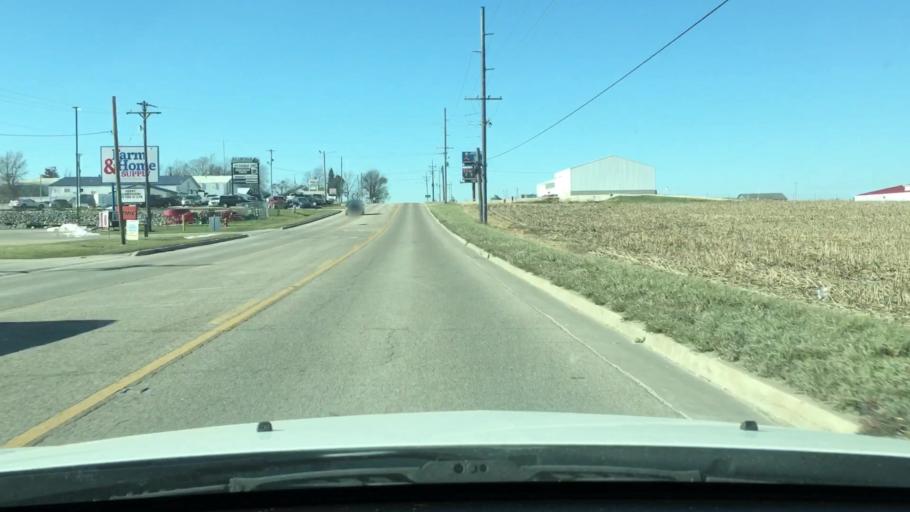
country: US
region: Illinois
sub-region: Pike County
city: Pittsfield
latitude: 39.6047
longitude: -90.8423
